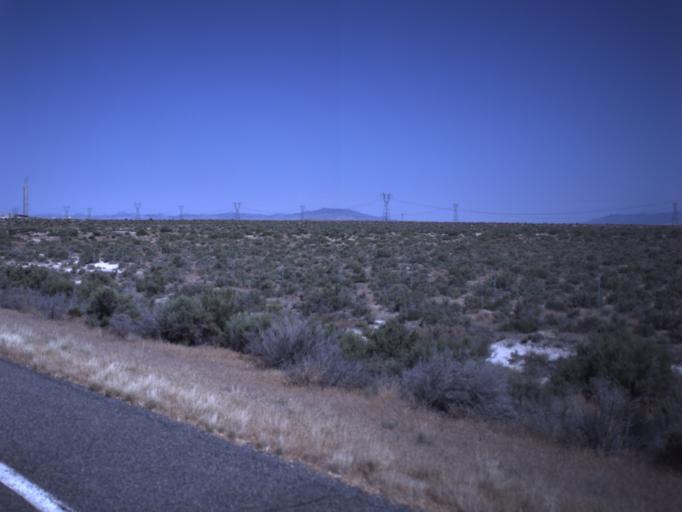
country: US
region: Utah
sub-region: Millard County
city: Delta
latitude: 39.4844
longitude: -112.5285
